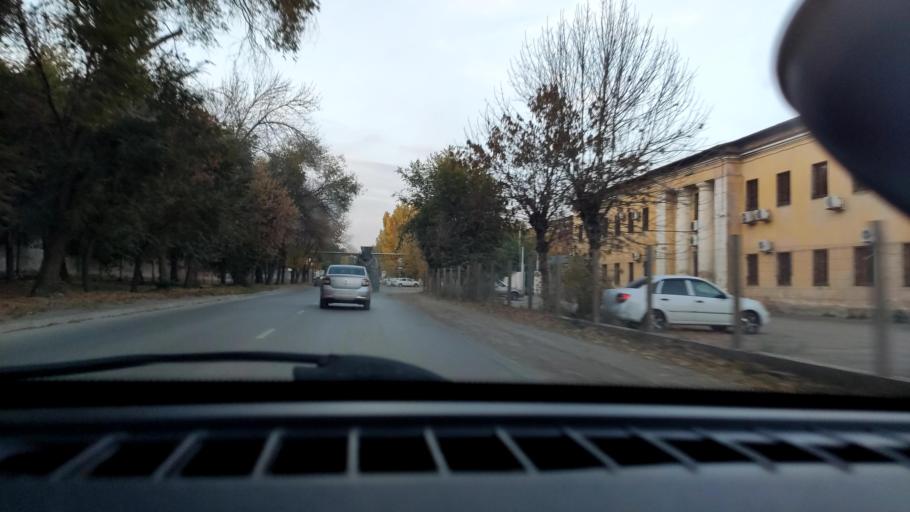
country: RU
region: Samara
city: Samara
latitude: 53.1860
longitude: 50.2446
